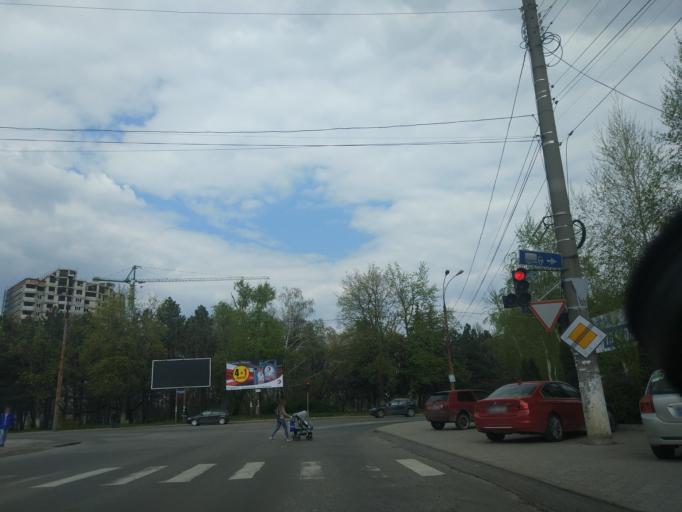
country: MD
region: Chisinau
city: Chisinau
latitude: 46.9883
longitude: 28.8702
